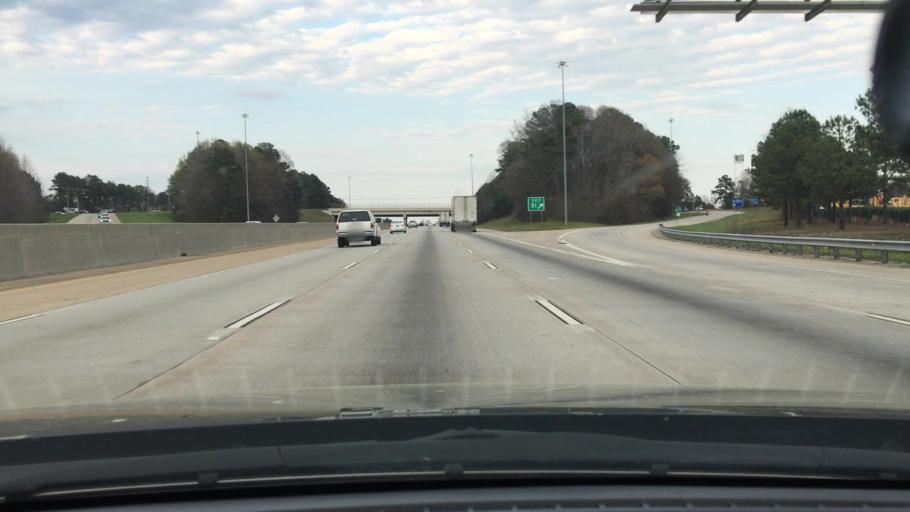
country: US
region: Georgia
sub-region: Fulton County
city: Palmetto
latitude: 33.4413
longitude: -84.6978
